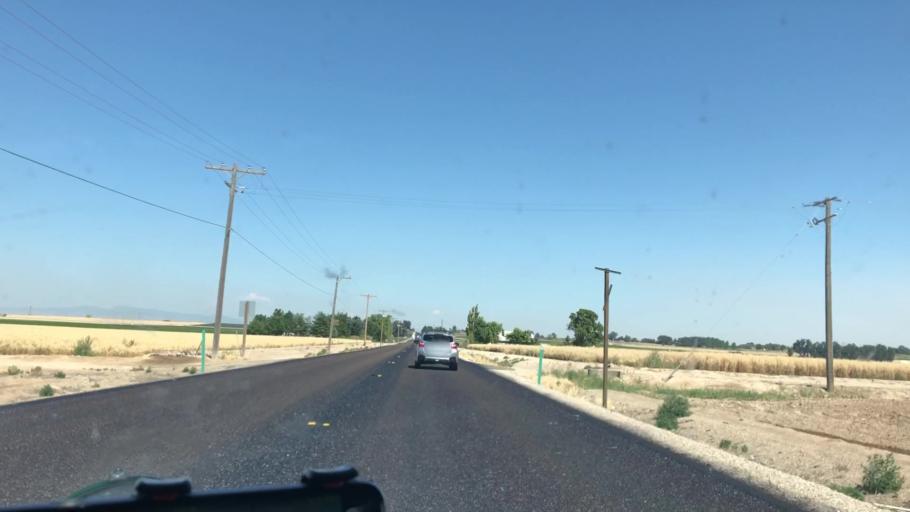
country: US
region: Idaho
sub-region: Canyon County
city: Caldwell
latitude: 43.6034
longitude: -116.7484
